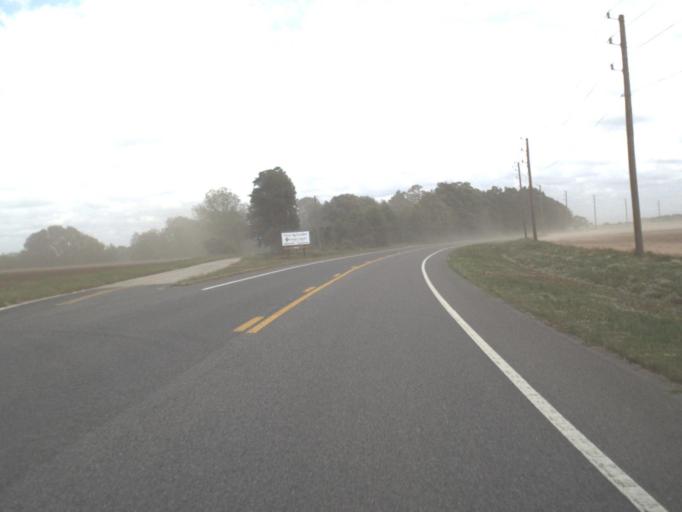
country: US
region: Florida
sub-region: Santa Rosa County
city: Point Baker
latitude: 30.8064
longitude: -87.1002
